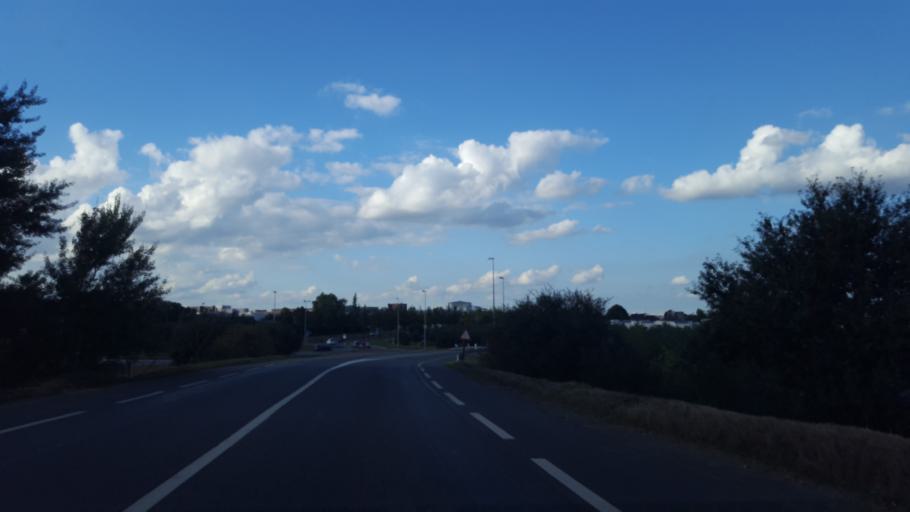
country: FR
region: Brittany
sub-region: Departement d'Ille-et-Vilaine
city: Saint-Jacques-de-la-Lande
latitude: 48.0727
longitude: -1.7111
